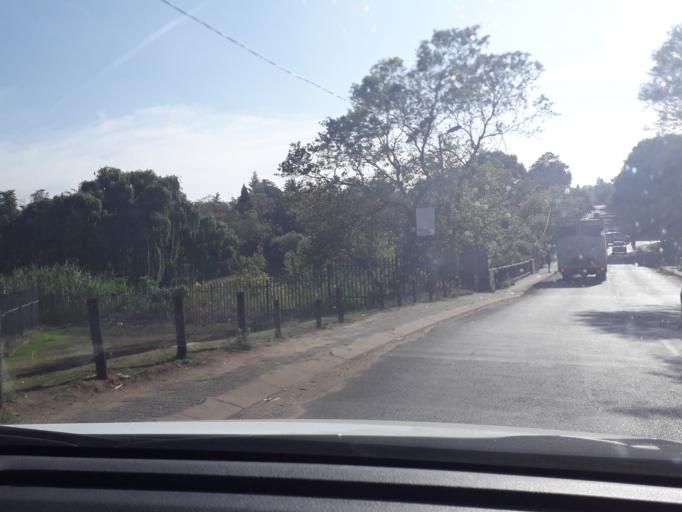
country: ZA
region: Gauteng
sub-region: City of Johannesburg Metropolitan Municipality
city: Diepsloot
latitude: -26.0335
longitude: 27.9837
